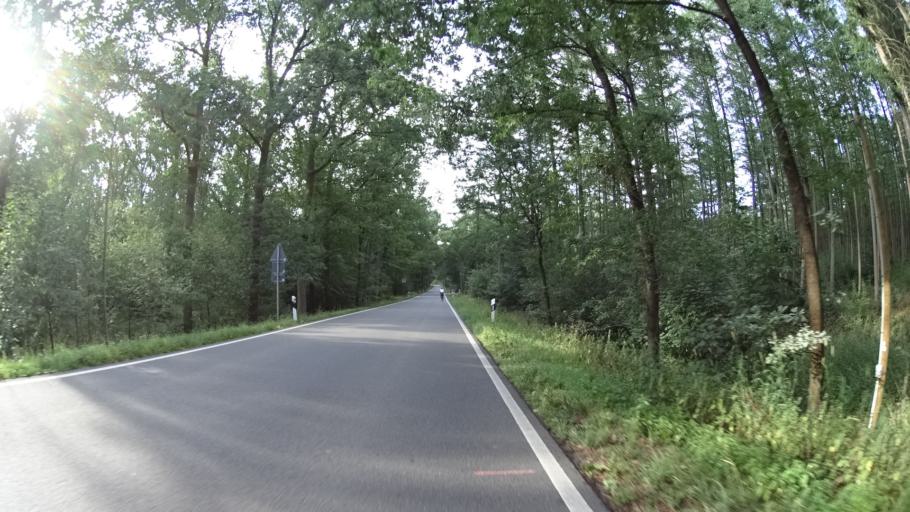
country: DE
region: Lower Saxony
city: Undeloh
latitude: 53.1661
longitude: 9.8951
